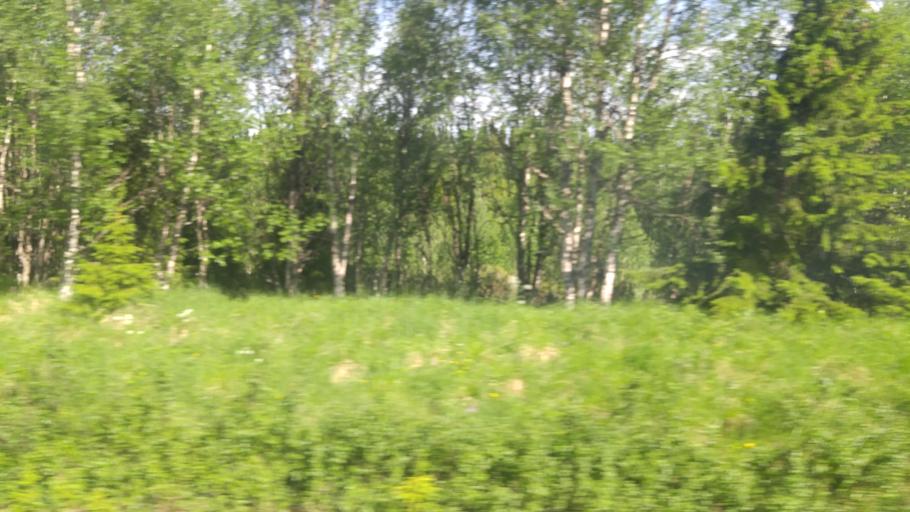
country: SE
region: Jaemtland
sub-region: Are Kommun
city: Are
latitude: 63.3744
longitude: 12.7323
